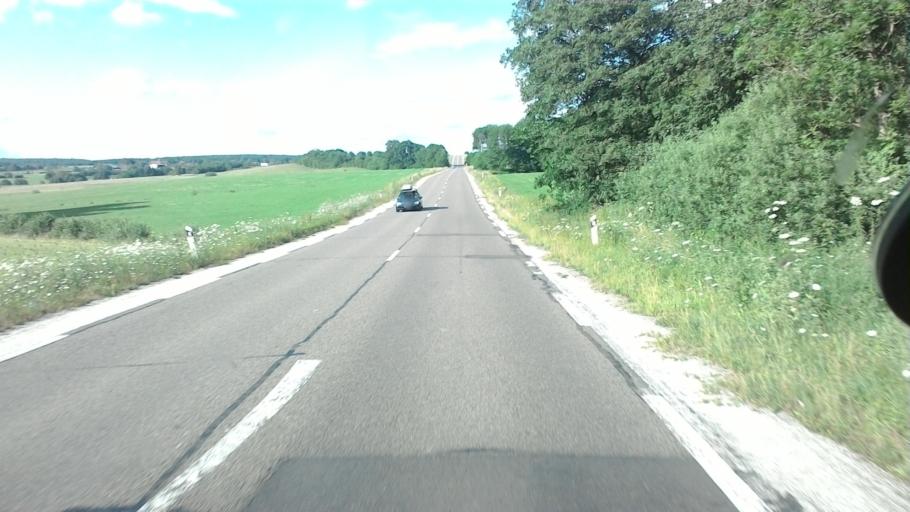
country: FR
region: Franche-Comte
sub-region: Departement de la Haute-Saone
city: Luxeuil-les-Bains
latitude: 47.7102
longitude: 6.2963
